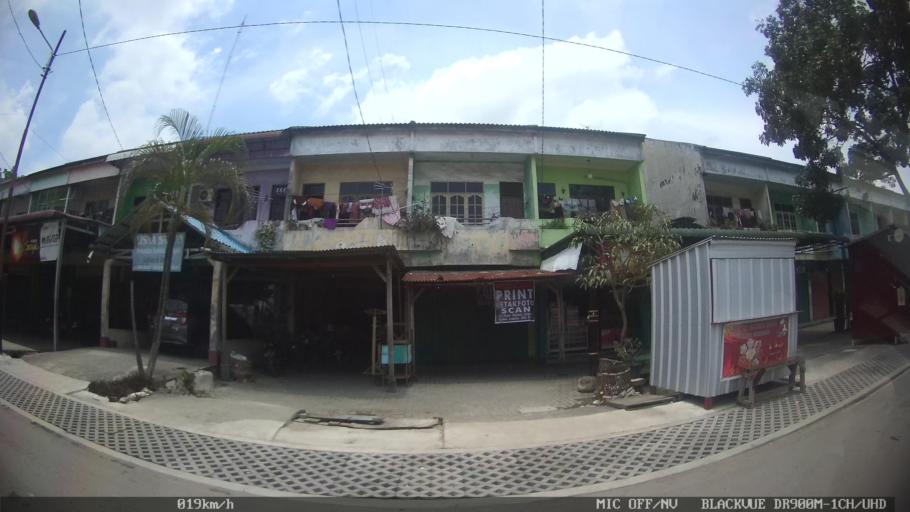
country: ID
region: North Sumatra
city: Labuhan Deli
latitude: 3.6920
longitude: 98.6936
